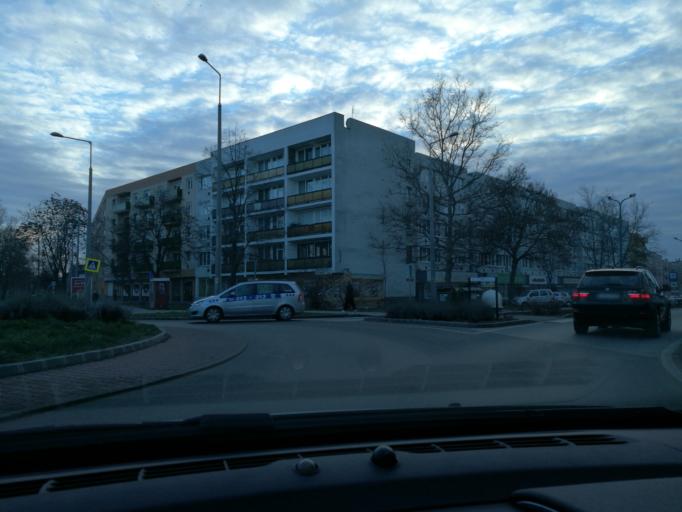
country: HU
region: Szabolcs-Szatmar-Bereg
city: Nyiregyhaza
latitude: 47.9483
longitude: 21.7156
